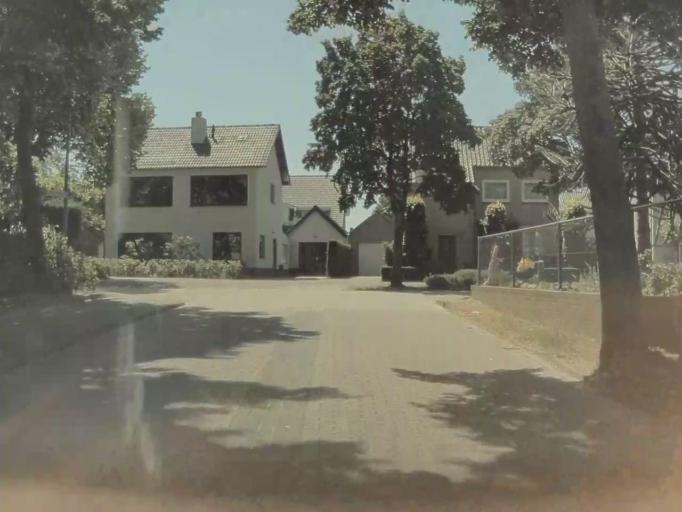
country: NL
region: North Brabant
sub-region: Gemeente 's-Hertogenbosch
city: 's-Hertogenbosch
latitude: 51.7198
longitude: 5.3605
